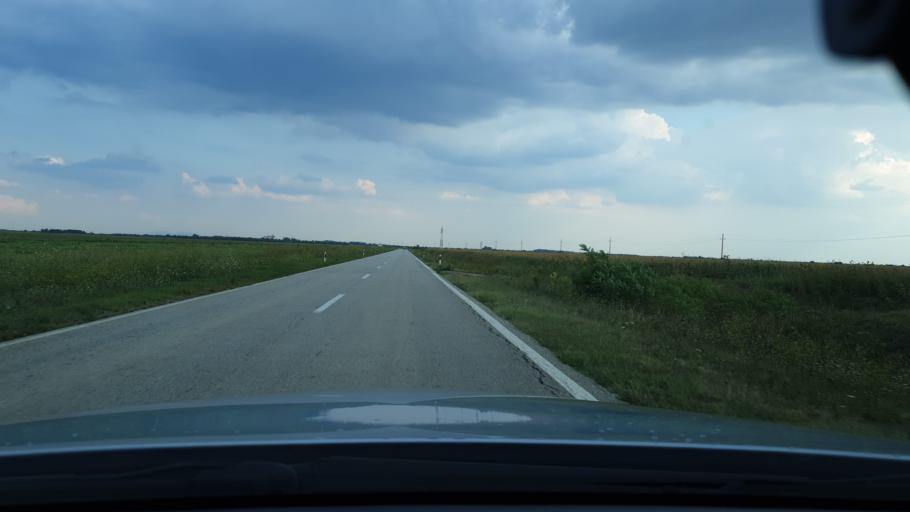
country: RS
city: Boka
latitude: 45.3408
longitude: 20.8616
